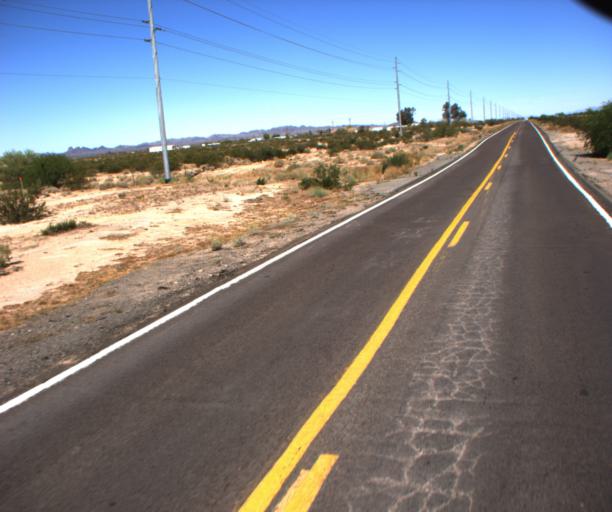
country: US
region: Arizona
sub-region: La Paz County
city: Salome
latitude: 33.8645
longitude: -113.9230
